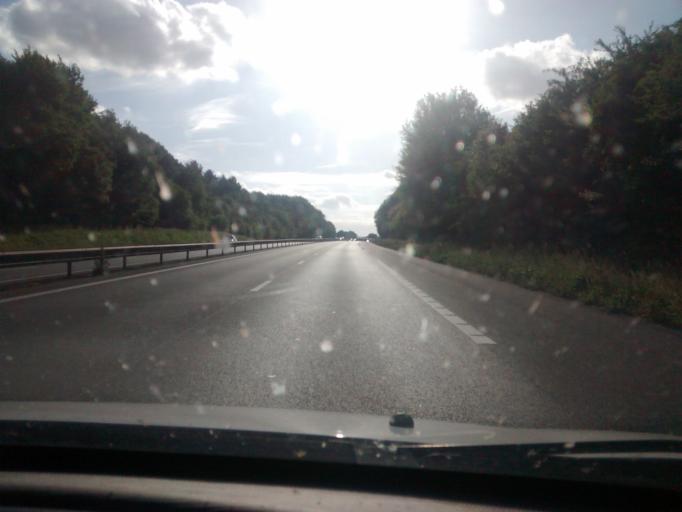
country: FR
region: Brittany
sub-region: Departement d'Ille-et-Vilaine
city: Louvigne-de-Bais
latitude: 48.0767
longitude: -1.3100
